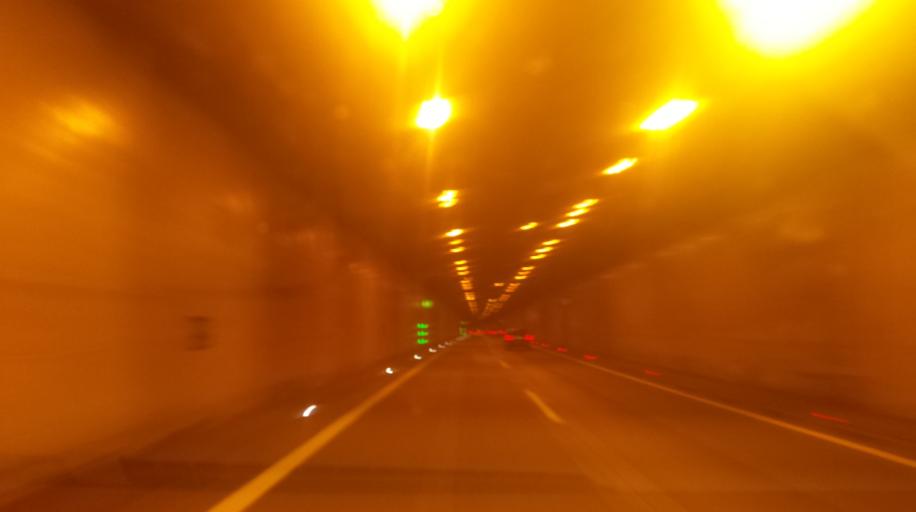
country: AT
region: Upper Austria
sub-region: Wels-Land
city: Steinhaus
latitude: 48.1189
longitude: 14.0088
